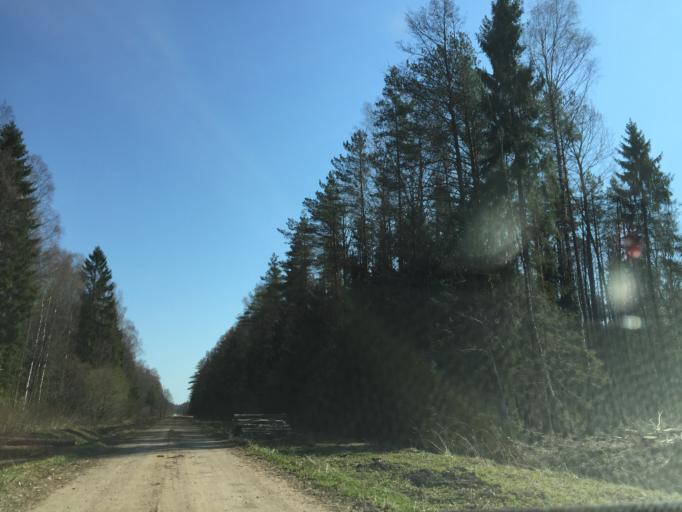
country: EE
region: Tartu
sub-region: Tartu linn
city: Tartu
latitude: 58.5286
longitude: 26.9019
